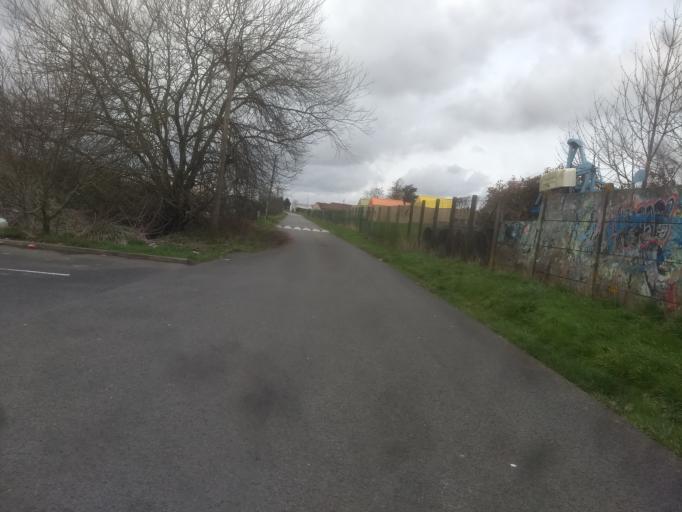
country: FR
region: Nord-Pas-de-Calais
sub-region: Departement du Pas-de-Calais
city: Sainte-Catherine
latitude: 50.3120
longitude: 2.7587
